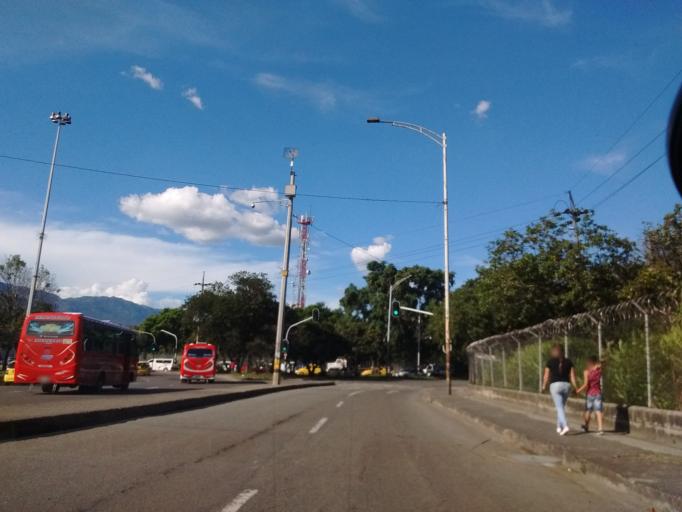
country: CO
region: Antioquia
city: Medellin
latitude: 6.2758
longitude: -75.5722
